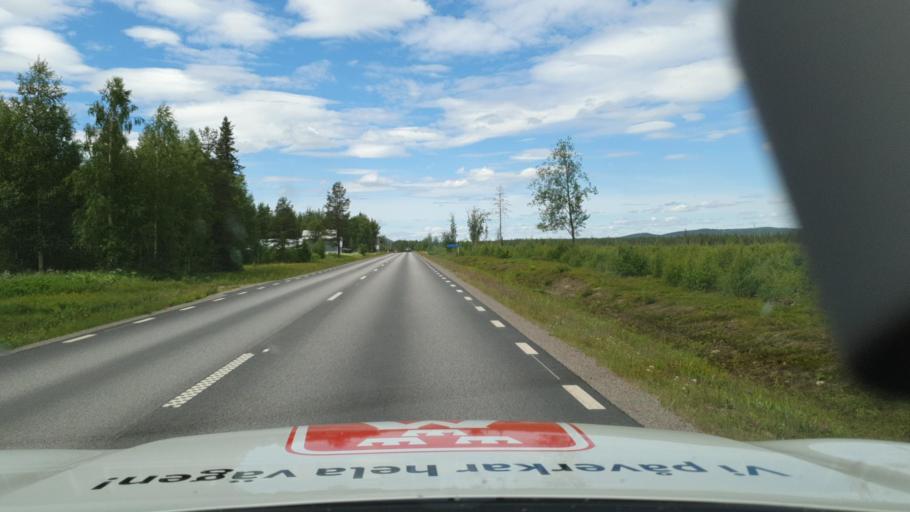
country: SE
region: Vaesterbotten
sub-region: Norsjo Kommun
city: Norsjoe
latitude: 65.2258
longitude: 19.7490
